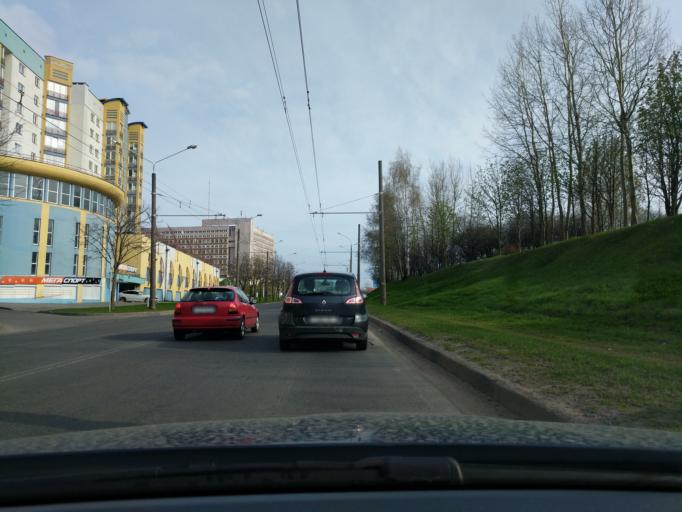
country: BY
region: Minsk
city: Novoye Medvezhino
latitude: 53.9051
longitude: 27.4629
